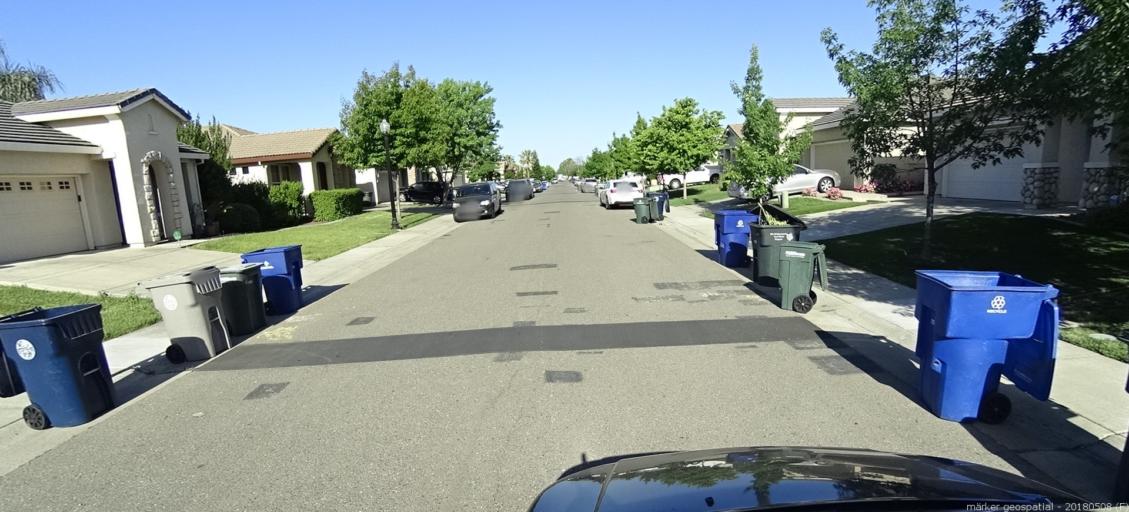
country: US
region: California
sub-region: Sacramento County
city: Elverta
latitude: 38.6841
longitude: -121.5011
